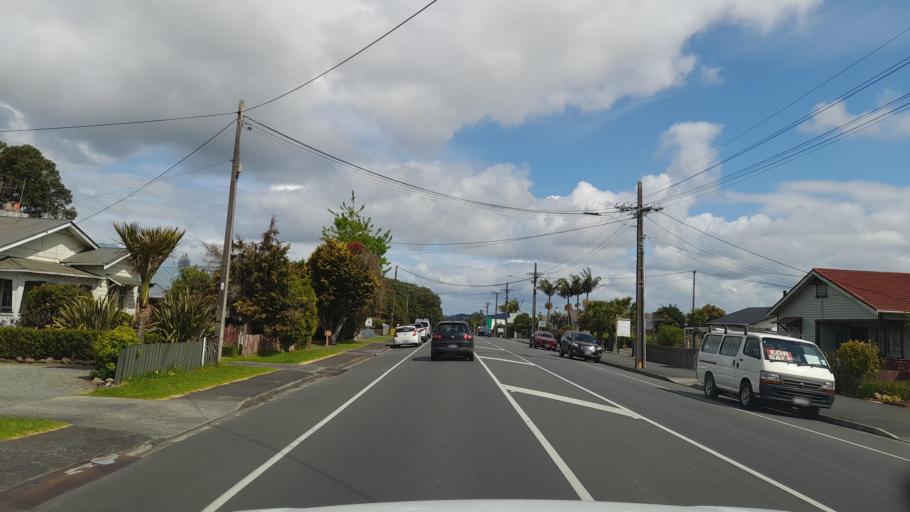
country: NZ
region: Northland
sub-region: Whangarei
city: Whangarei
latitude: -35.7120
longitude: 174.3223
